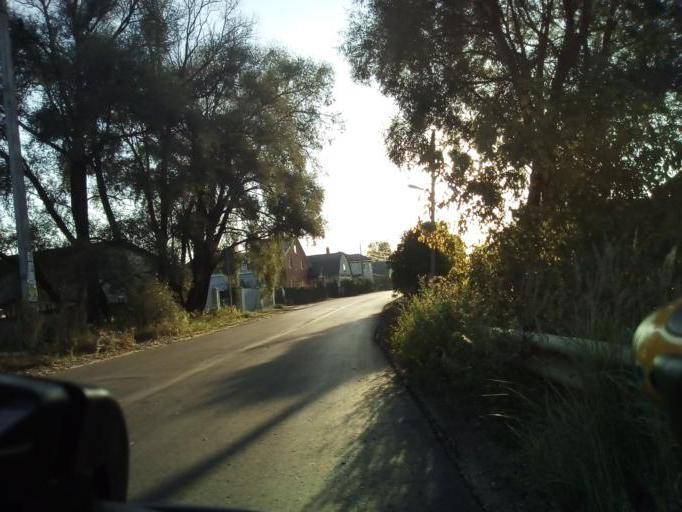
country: RU
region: Moskovskaya
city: Ramenskoye
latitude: 55.6131
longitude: 38.2984
